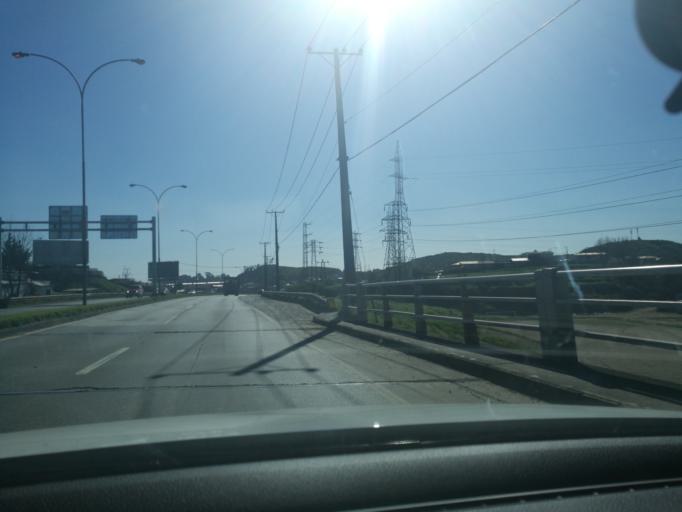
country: CL
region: Biobio
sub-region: Provincia de Concepcion
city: Concepcion
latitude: -36.8061
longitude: -73.0364
